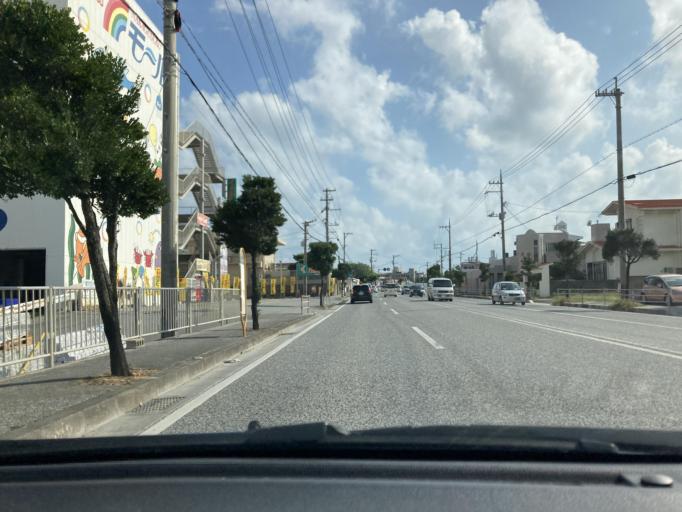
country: JP
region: Okinawa
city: Chatan
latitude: 26.2852
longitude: 127.8153
